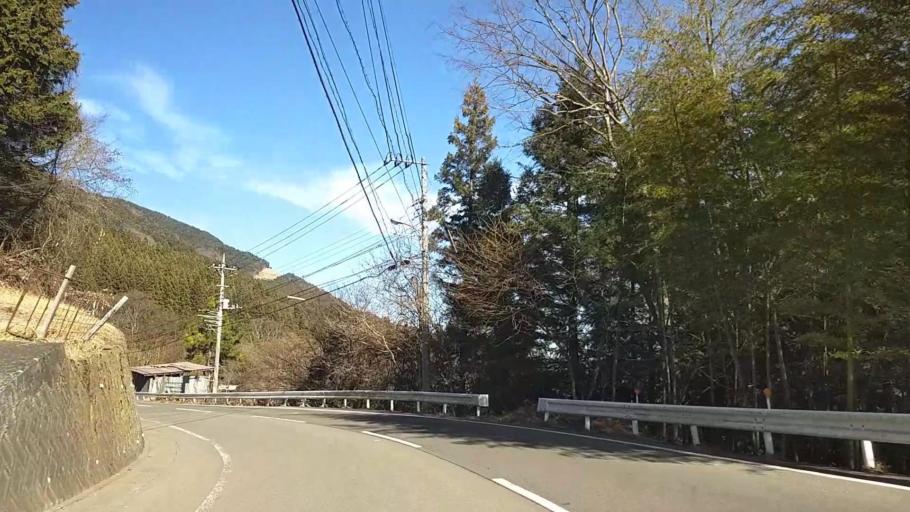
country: JP
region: Yamanashi
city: Otsuki
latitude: 35.5095
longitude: 138.9963
